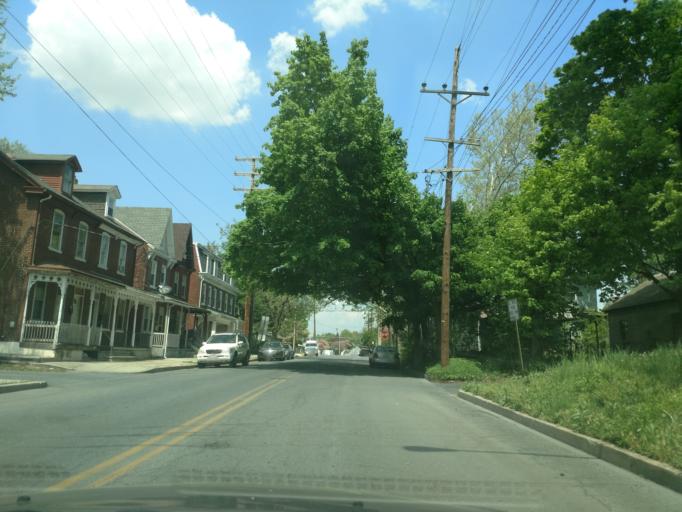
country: US
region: Pennsylvania
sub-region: Lebanon County
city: Hebron
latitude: 40.3449
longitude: -76.4042
